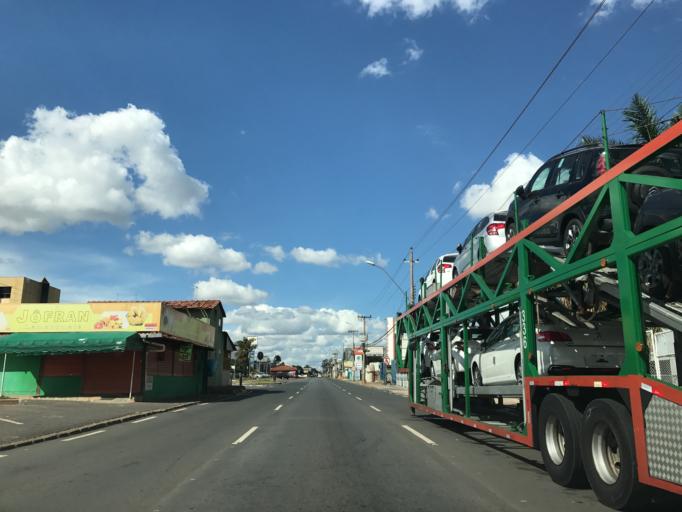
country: BR
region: Federal District
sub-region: Brasilia
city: Brasilia
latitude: -15.8033
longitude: -47.9645
